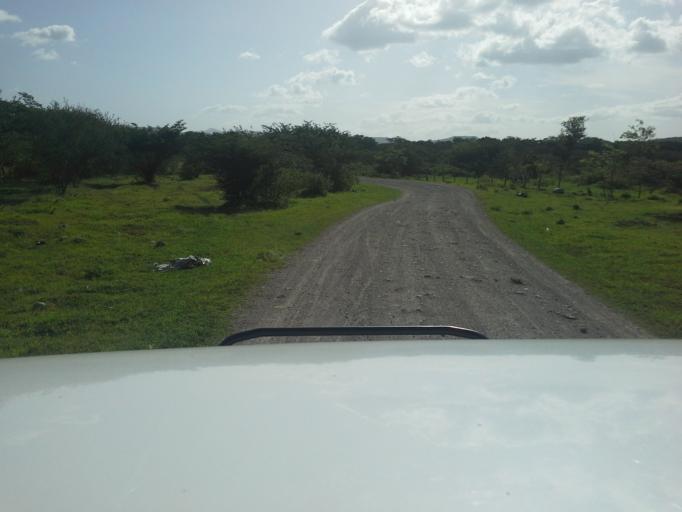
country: NI
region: Matagalpa
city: Ciudad Dario
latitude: 12.6644
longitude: -86.0579
